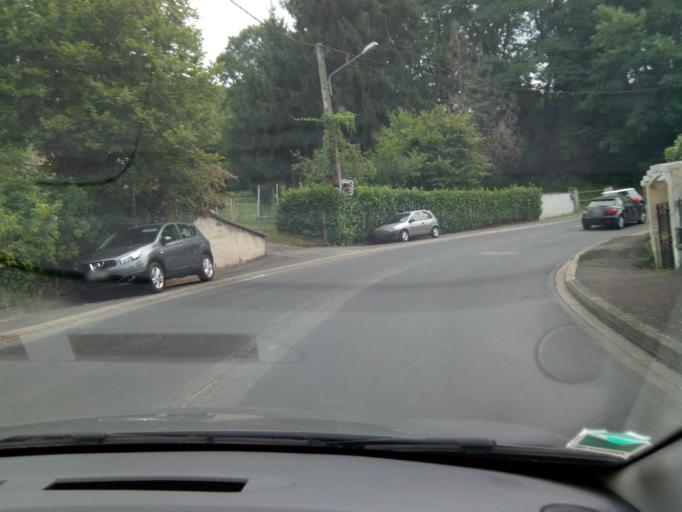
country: FR
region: Limousin
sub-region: Departement de la Correze
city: Brive-la-Gaillarde
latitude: 45.1481
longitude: 1.5465
